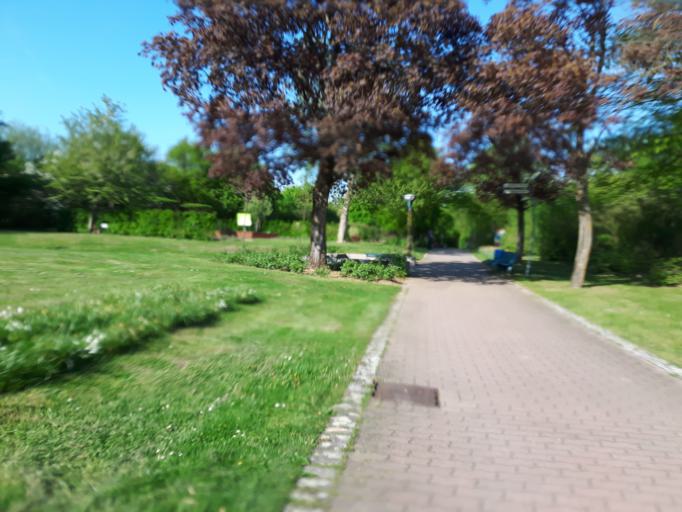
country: DE
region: Baden-Wuerttemberg
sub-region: Karlsruhe Region
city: Hockenheim
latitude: 49.3282
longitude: 8.5450
